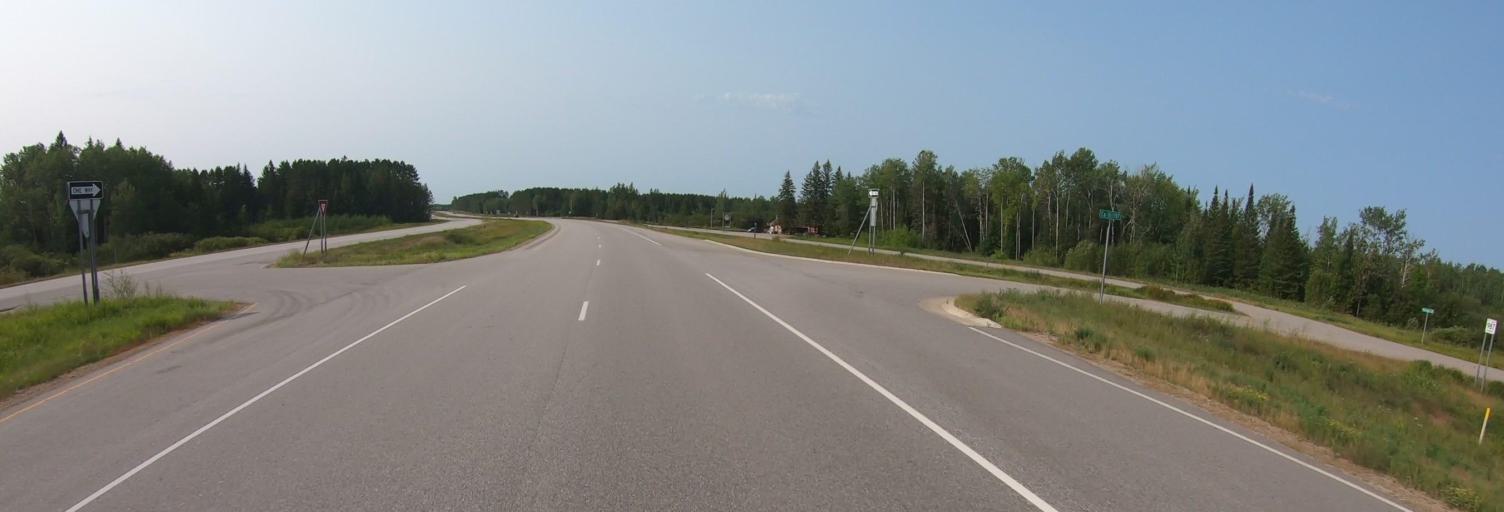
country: US
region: Minnesota
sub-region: Saint Louis County
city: Mountain Iron
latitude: 47.7376
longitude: -92.6509
